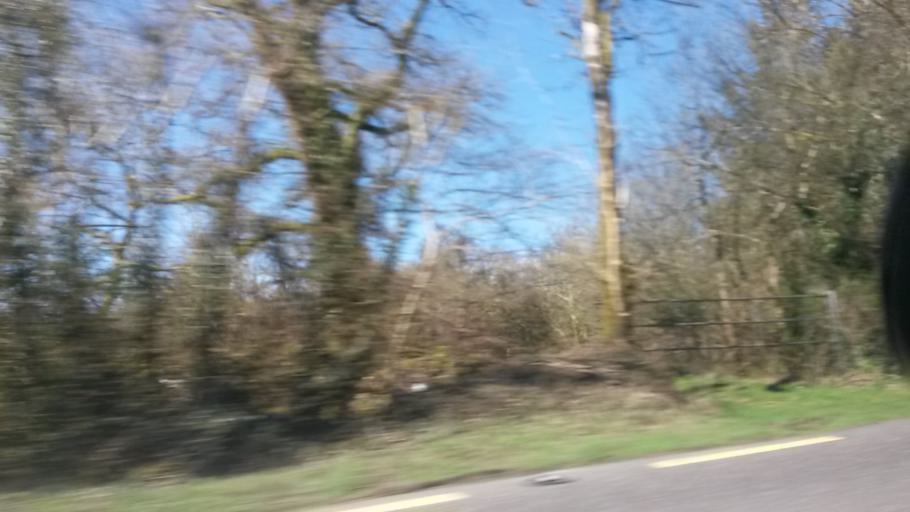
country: IE
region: Munster
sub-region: County Cork
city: Millstreet
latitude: 51.9476
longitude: -9.1779
